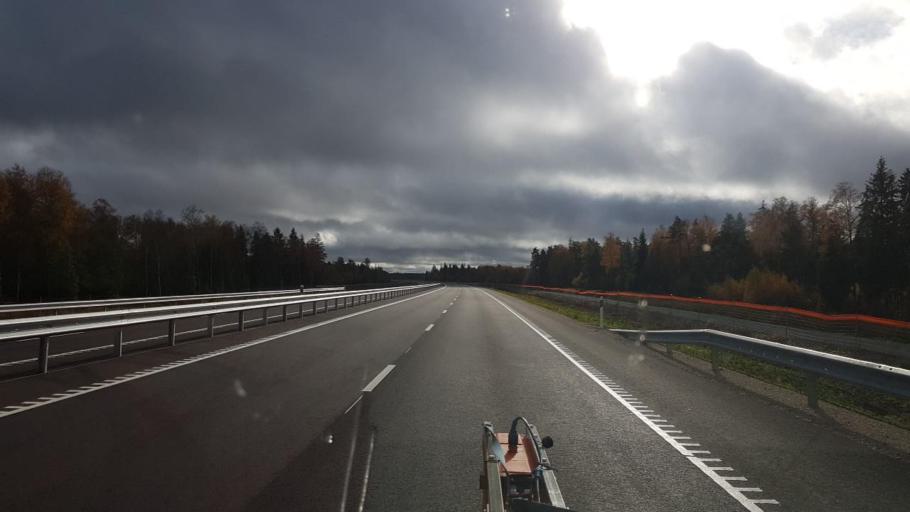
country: EE
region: Jaervamaa
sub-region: Paide linn
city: Paide
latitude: 59.0146
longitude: 25.5541
